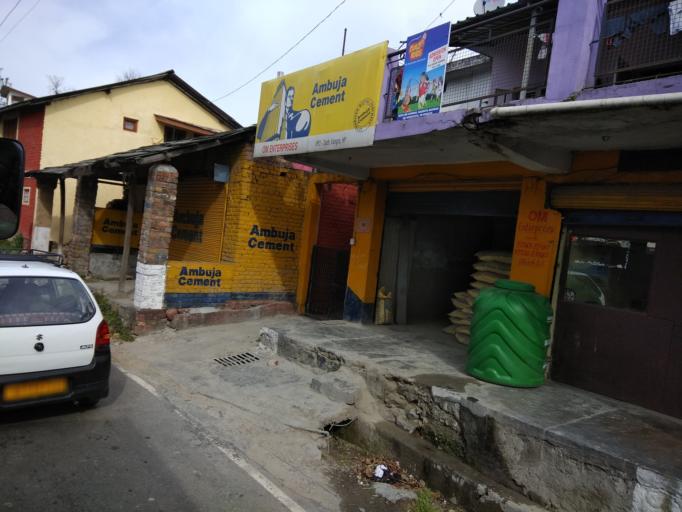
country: IN
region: Himachal Pradesh
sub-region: Kangra
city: Dharmsala
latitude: 32.1593
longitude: 76.4097
